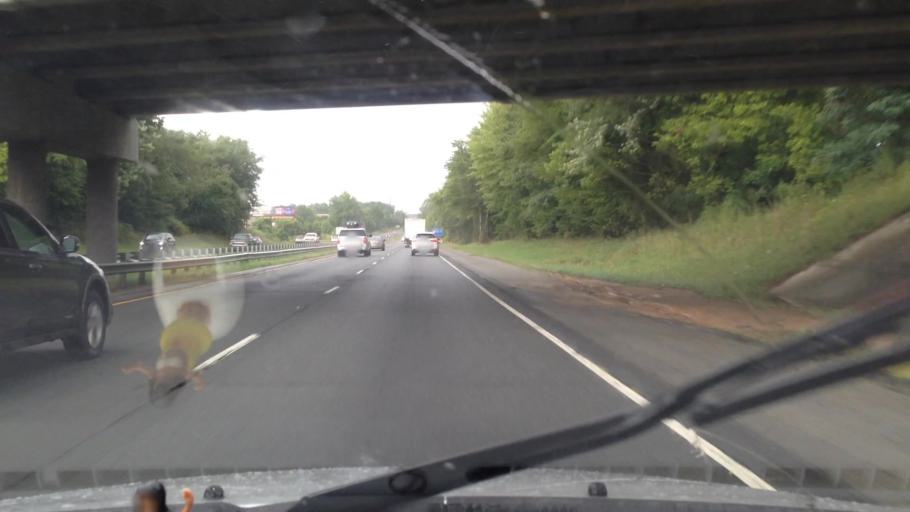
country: US
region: North Carolina
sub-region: Forsyth County
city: Kernersville
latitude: 36.1103
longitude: -80.0782
